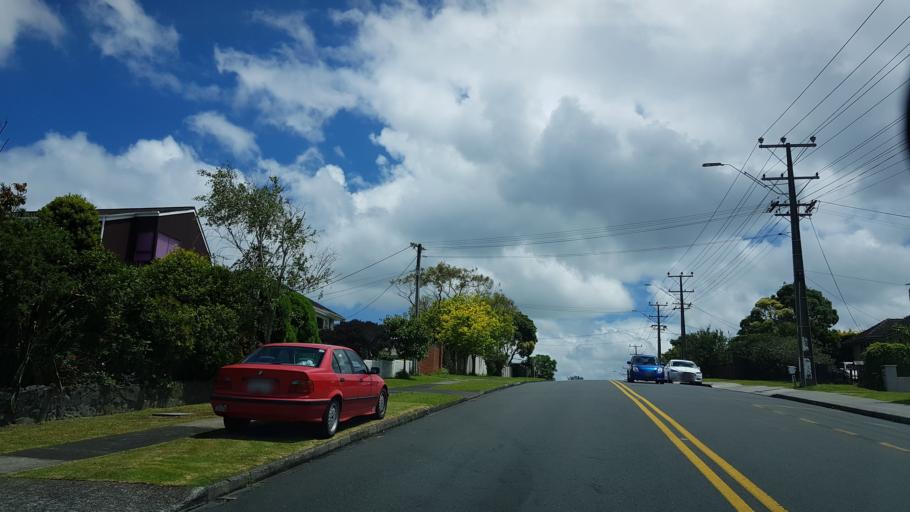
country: NZ
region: Auckland
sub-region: Auckland
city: North Shore
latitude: -36.7981
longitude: 174.7402
